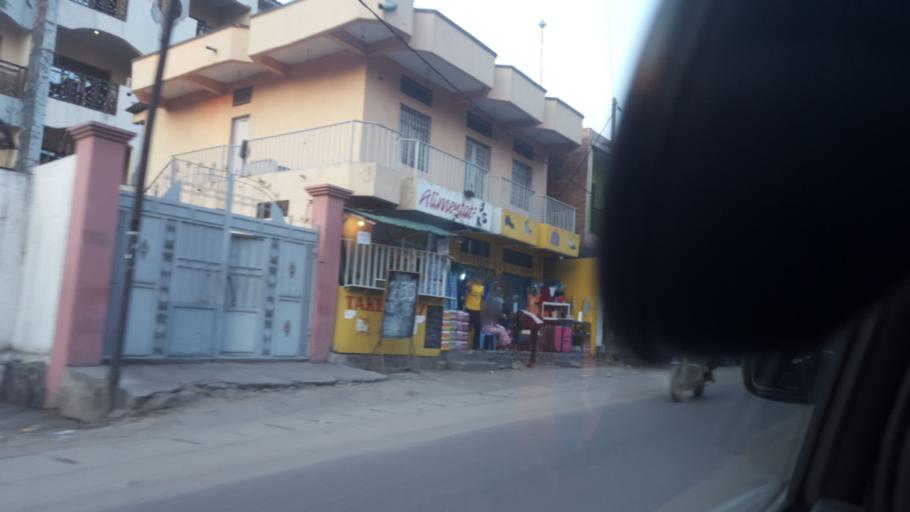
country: CD
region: Kinshasa
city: Kinshasa
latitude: -4.3520
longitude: 15.3294
